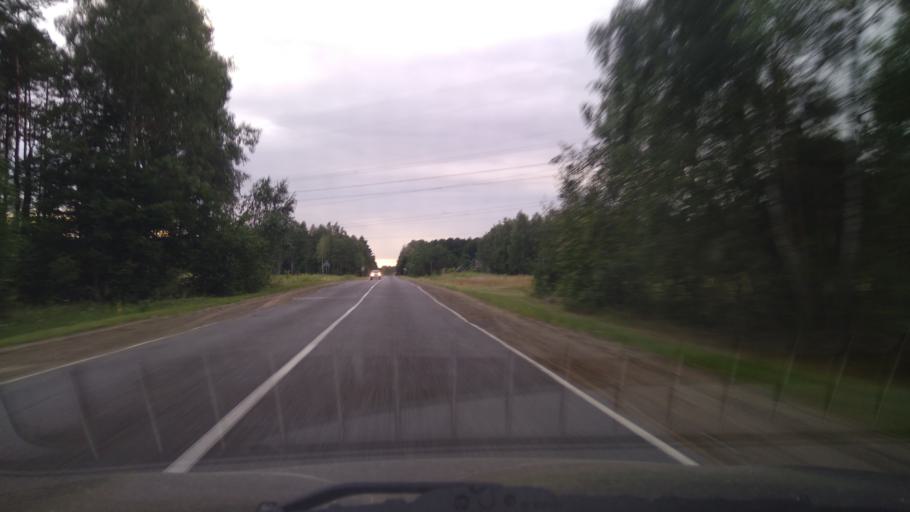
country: BY
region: Brest
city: Byaroza
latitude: 52.4136
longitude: 24.9892
